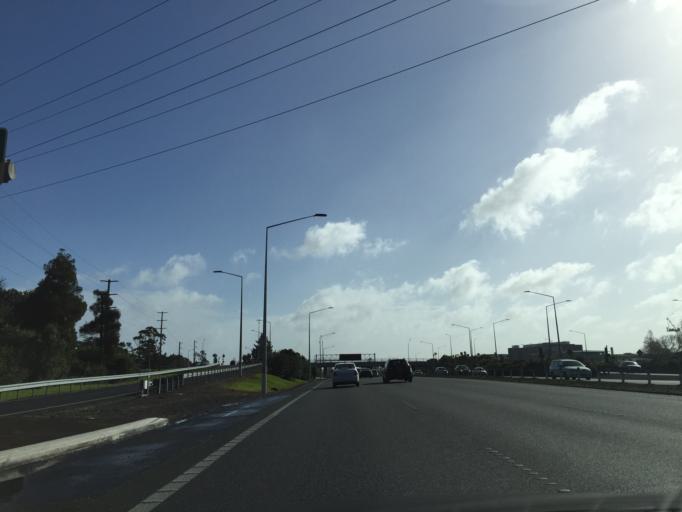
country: NZ
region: Auckland
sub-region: Auckland
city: North Shore
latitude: -36.7905
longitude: 174.7541
